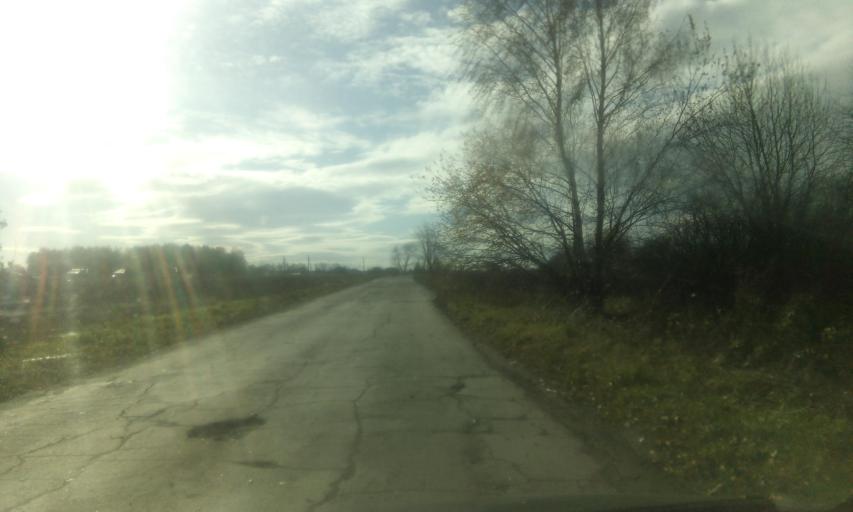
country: RU
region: Tula
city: Dubovka
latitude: 53.9438
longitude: 38.0360
